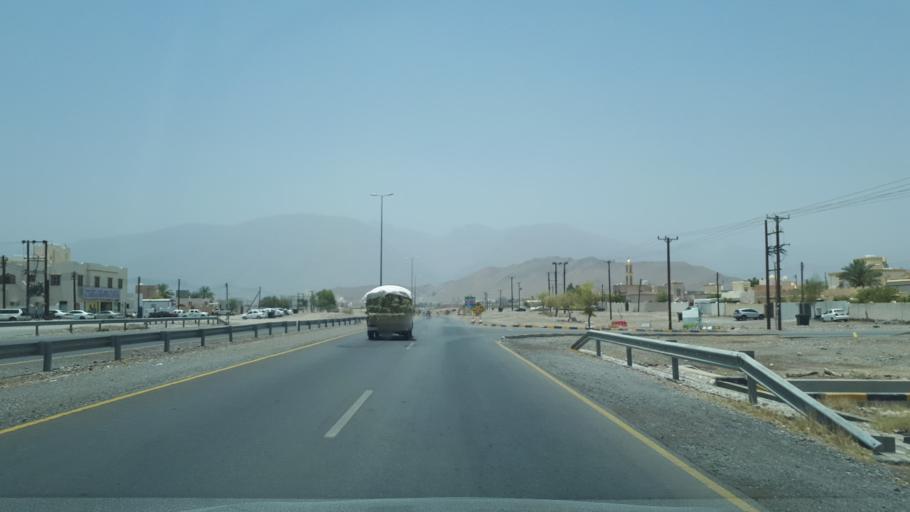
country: OM
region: Al Batinah
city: Rustaq
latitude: 23.4480
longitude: 57.4324
